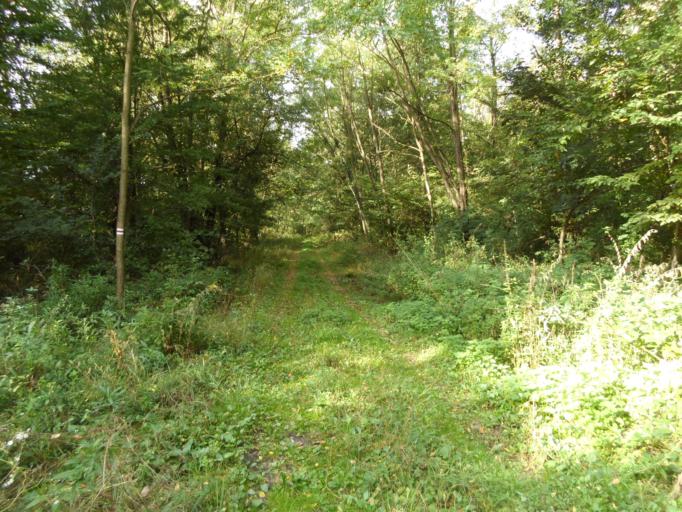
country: HU
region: Veszprem
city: Devecser
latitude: 47.2050
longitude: 17.4575
